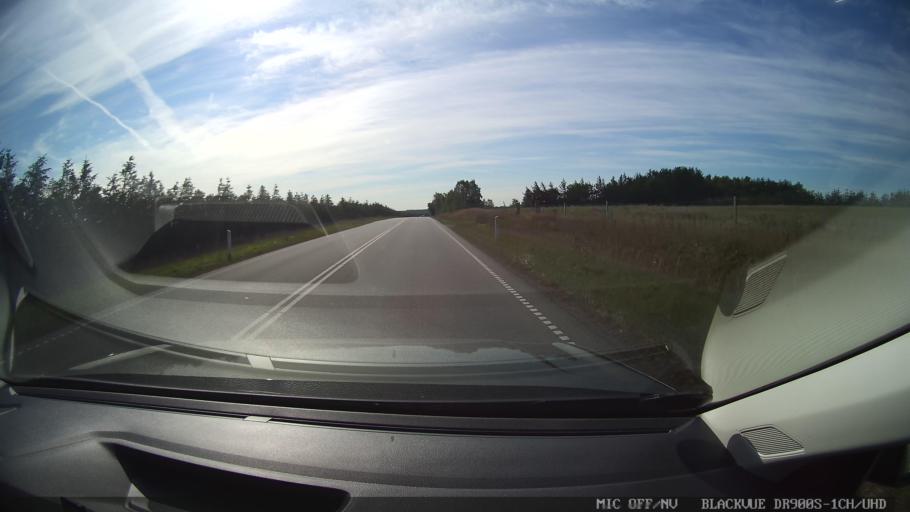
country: DK
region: North Denmark
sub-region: Mariagerfjord Kommune
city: Hadsund
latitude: 56.7654
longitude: 10.0643
